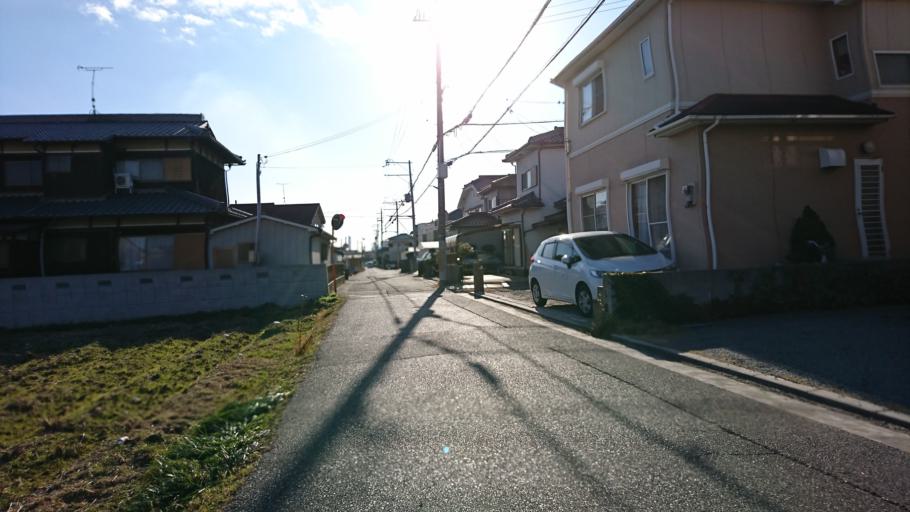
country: JP
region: Hyogo
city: Kakogawacho-honmachi
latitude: 34.7457
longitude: 134.8476
